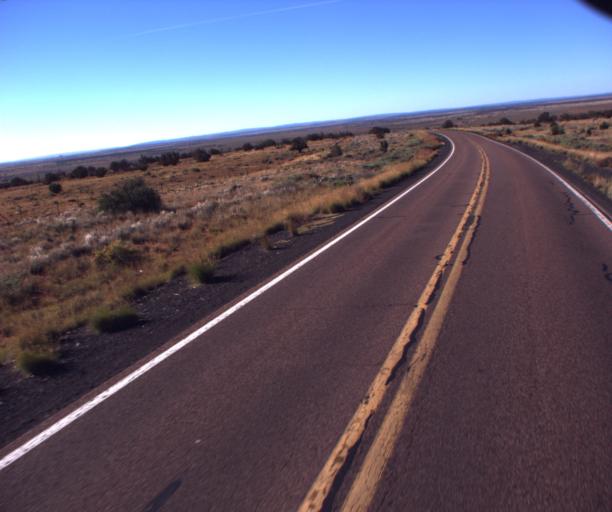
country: US
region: Arizona
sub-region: Navajo County
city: Snowflake
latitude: 34.6413
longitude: -110.3569
